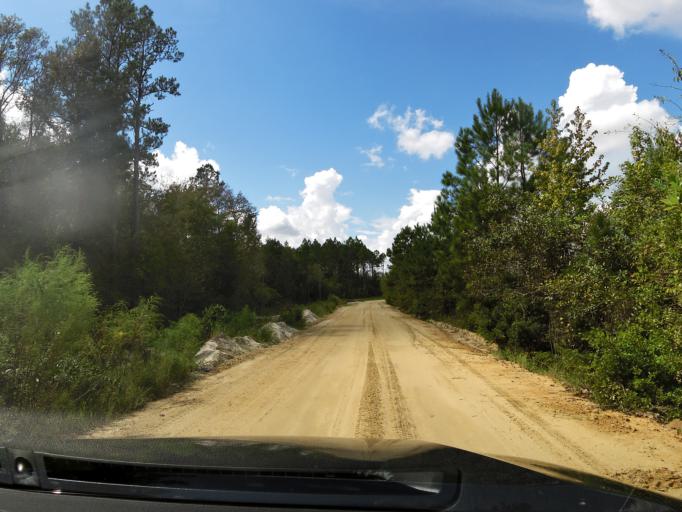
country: US
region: Georgia
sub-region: Brantley County
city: Nahunta
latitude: 31.0917
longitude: -82.0192
